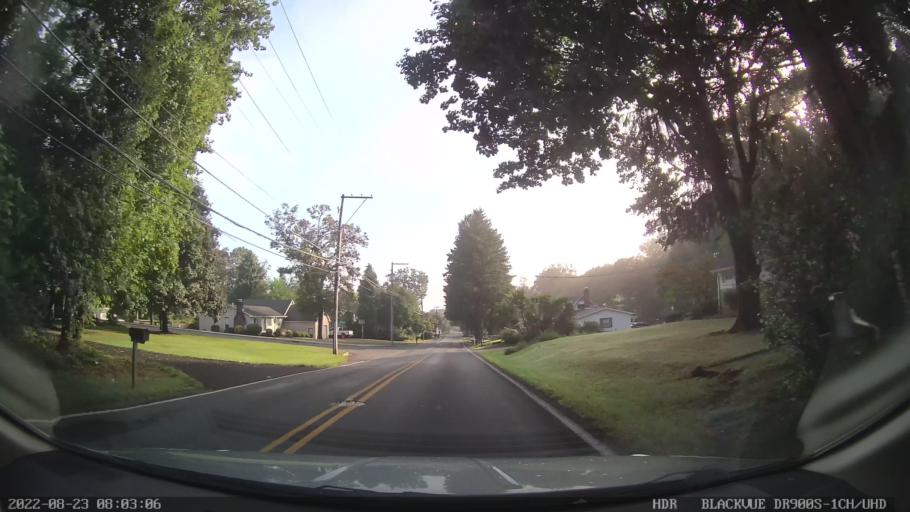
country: US
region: Pennsylvania
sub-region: Lehigh County
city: Wescosville
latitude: 40.5578
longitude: -75.5361
